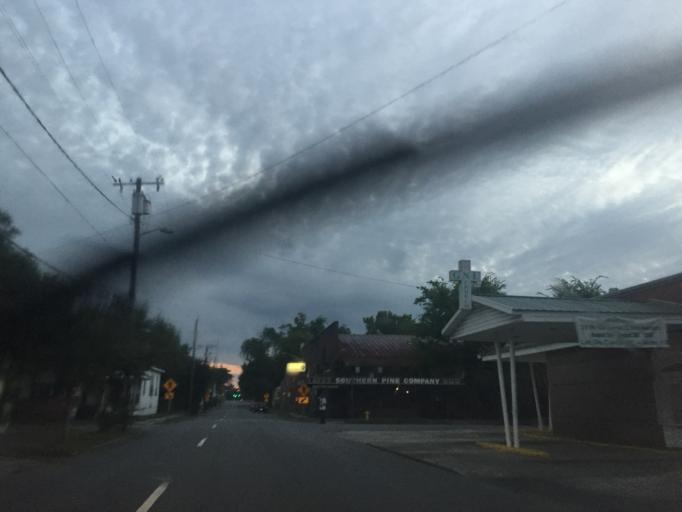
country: US
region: Georgia
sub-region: Chatham County
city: Savannah
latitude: 32.0567
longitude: -81.0923
